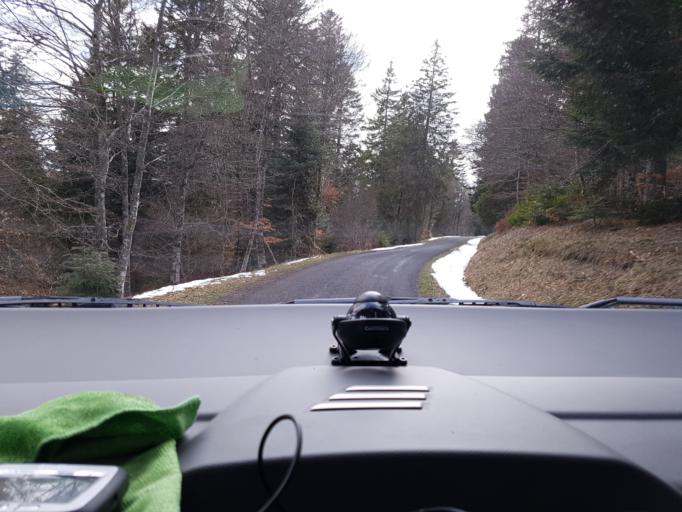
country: FR
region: Midi-Pyrenees
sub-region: Departement de l'Aveyron
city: Laguiole
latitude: 44.6513
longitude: 2.9458
